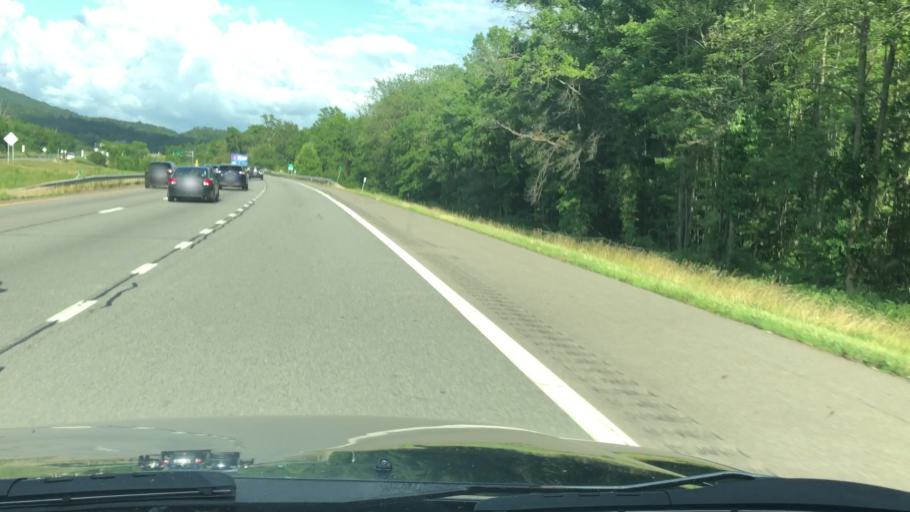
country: US
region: New York
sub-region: Dutchess County
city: Fishkill
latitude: 41.5223
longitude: -73.9024
